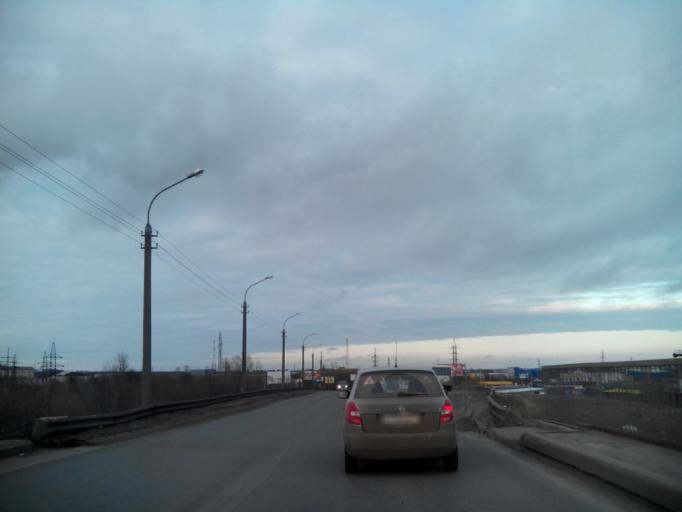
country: RU
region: Arkhangelskaya
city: Arkhangel'sk
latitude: 64.5664
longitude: 40.5606
